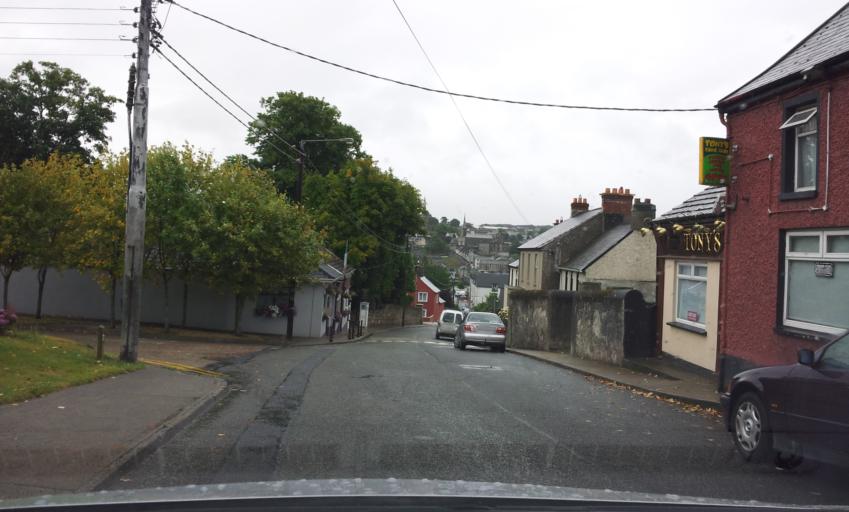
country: IE
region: Leinster
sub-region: Loch Garman
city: New Ross
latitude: 52.3986
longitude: -6.9524
